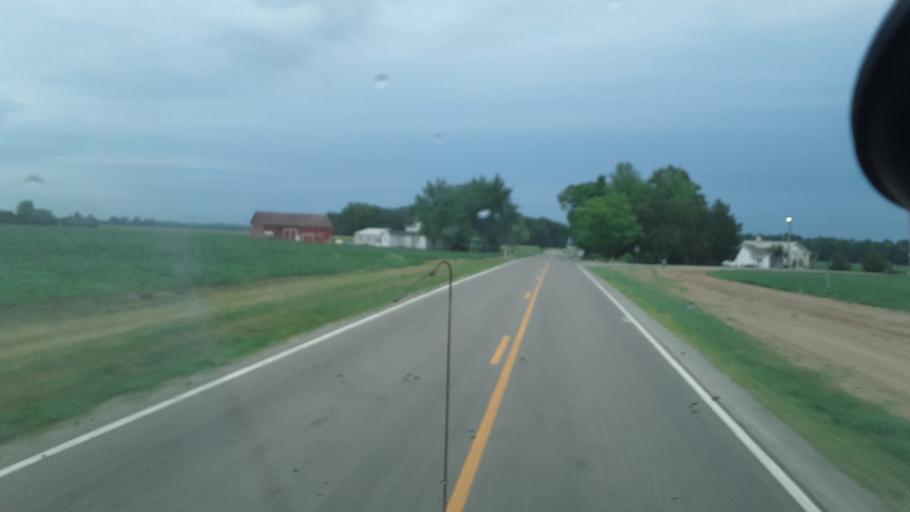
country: US
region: Ohio
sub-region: Defiance County
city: Hicksville
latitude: 41.2826
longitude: -84.7481
